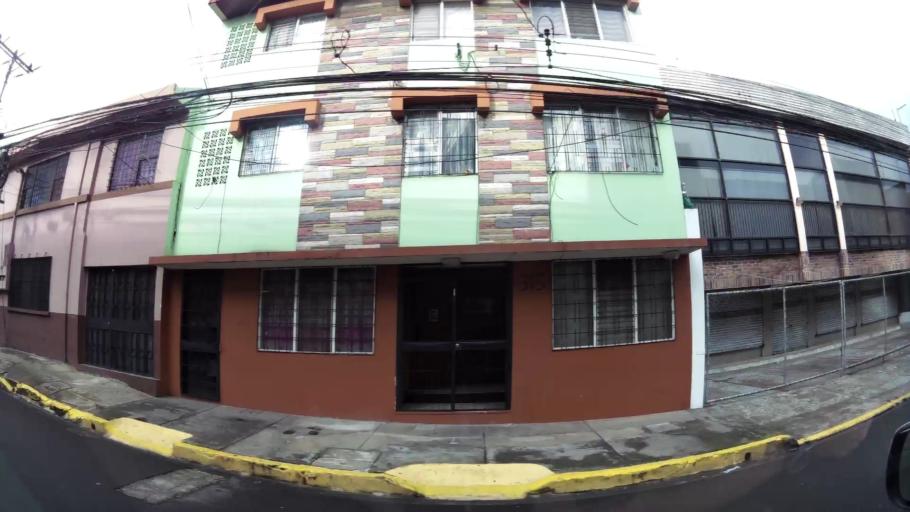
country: CR
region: San Jose
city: San Jose
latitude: 9.9367
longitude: -84.0882
